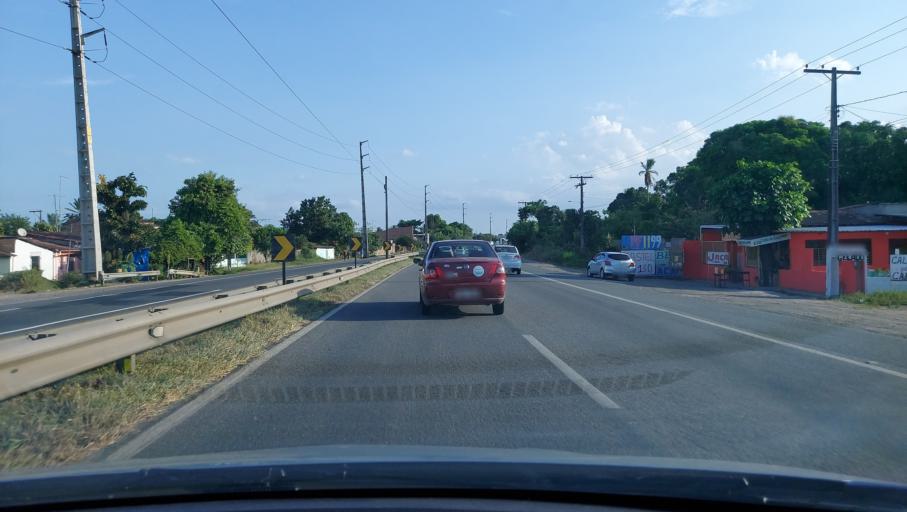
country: BR
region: Bahia
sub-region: Conceicao Do Jacuipe
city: Conceicao do Jacuipe
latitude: -12.4073
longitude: -38.7528
